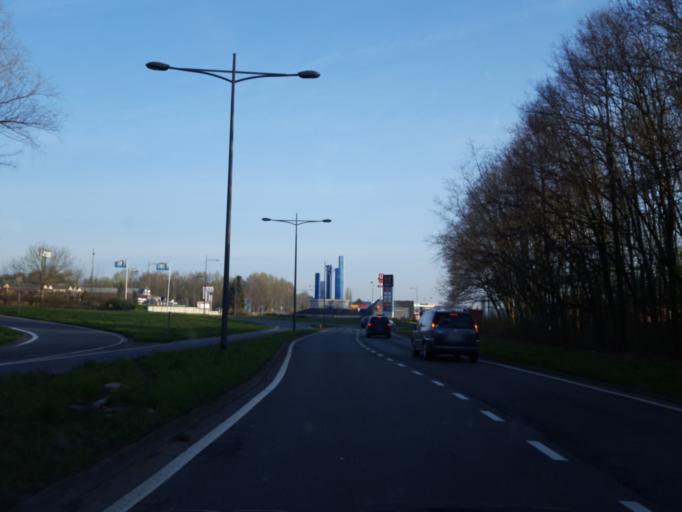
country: BE
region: Wallonia
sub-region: Province du Brabant Wallon
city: Nivelles
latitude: 50.5870
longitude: 4.3092
